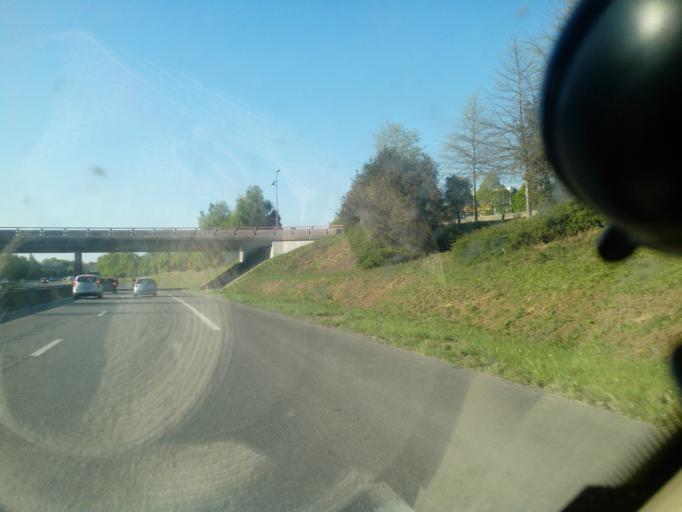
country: FR
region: Pays de la Loire
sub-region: Departement de la Loire-Atlantique
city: Orvault
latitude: 47.2510
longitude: -1.6207
